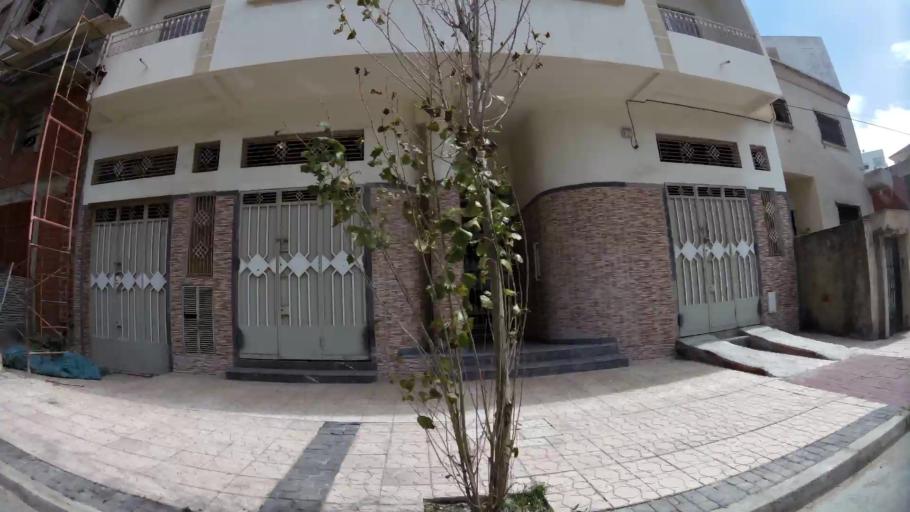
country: MA
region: Tanger-Tetouan
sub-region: Tanger-Assilah
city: Tangier
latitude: 35.7638
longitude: -5.8393
